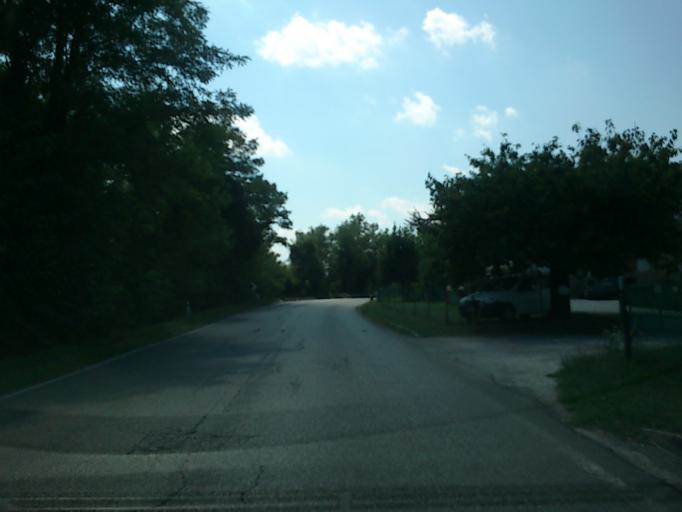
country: IT
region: The Marches
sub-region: Provincia di Pesaro e Urbino
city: Calcinelli
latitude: 43.7462
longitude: 12.9121
